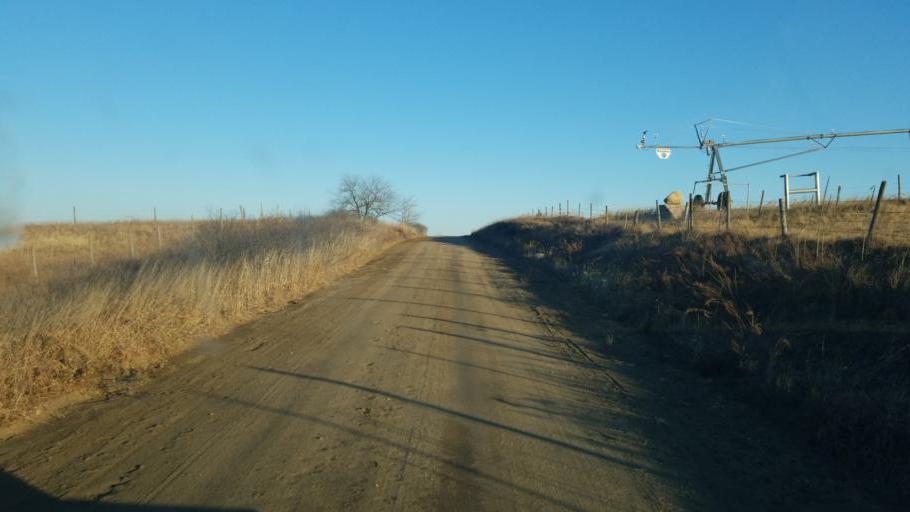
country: US
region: Nebraska
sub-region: Knox County
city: Center
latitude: 42.6040
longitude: -97.8378
